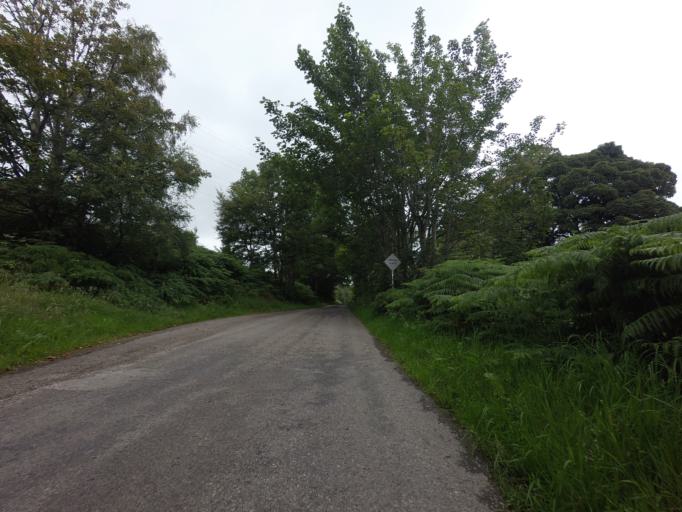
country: GB
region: Scotland
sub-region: Highland
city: Alness
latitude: 57.8935
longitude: -4.3752
